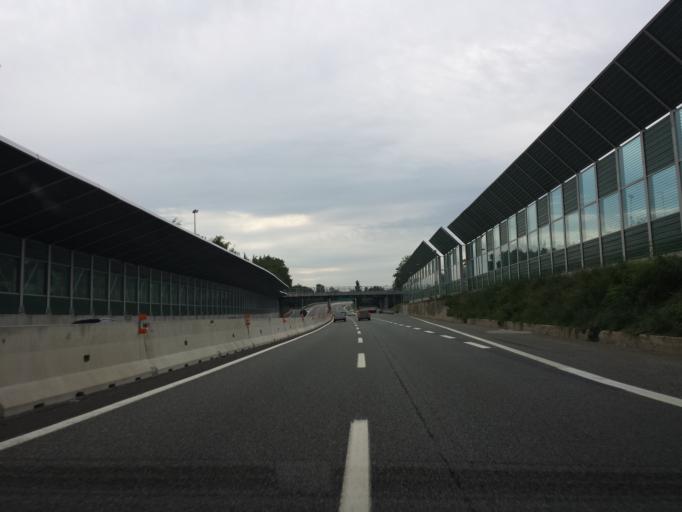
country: IT
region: Lombardy
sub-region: Provincia di Varese
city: Cavaria Con Premezzo
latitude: 45.6784
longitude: 8.7970
